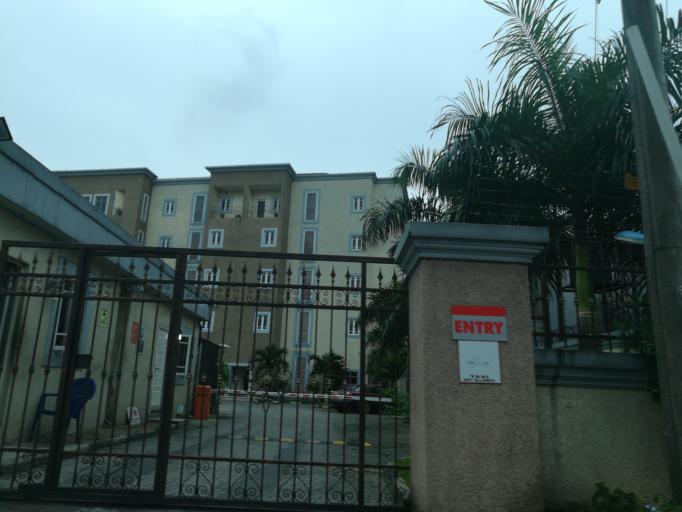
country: NG
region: Rivers
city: Port Harcourt
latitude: 4.8238
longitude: 6.9902
